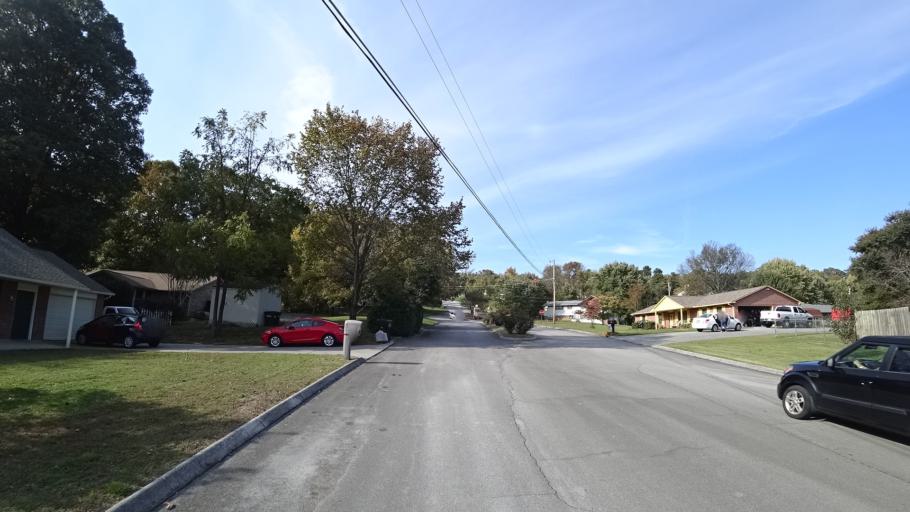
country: US
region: Tennessee
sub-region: Knox County
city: Farragut
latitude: 35.9135
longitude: -84.1658
